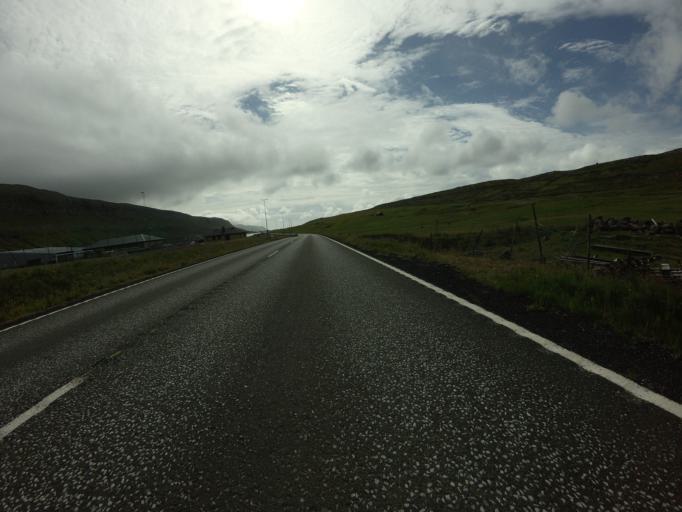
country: FO
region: Sandoy
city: Sandur
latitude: 61.8586
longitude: -6.8332
